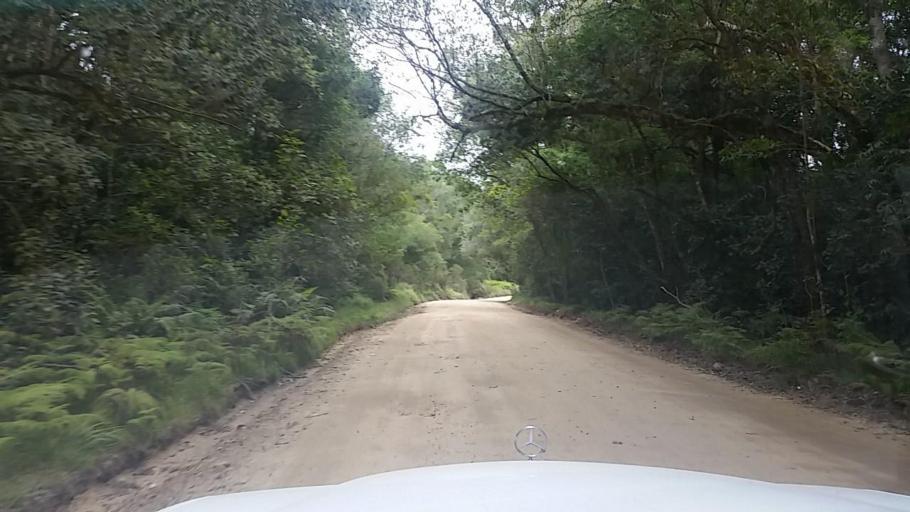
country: ZA
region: Western Cape
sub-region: Eden District Municipality
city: Knysna
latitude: -33.9438
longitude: 23.1587
